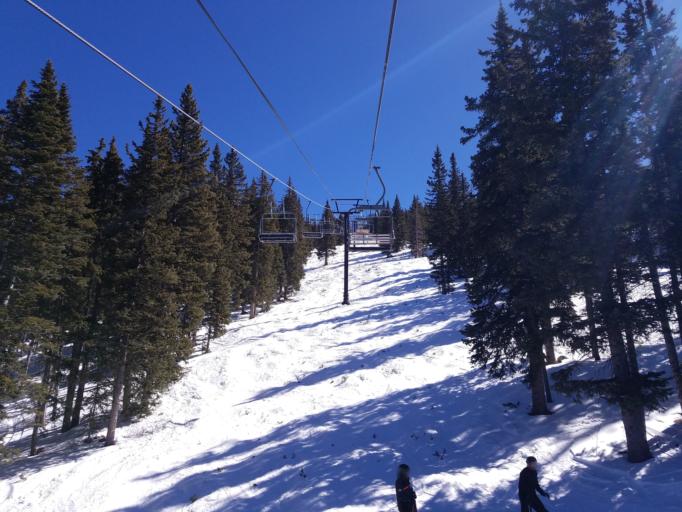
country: US
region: New Mexico
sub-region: Santa Fe County
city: Santa Fe
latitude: 35.7896
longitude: -105.7889
